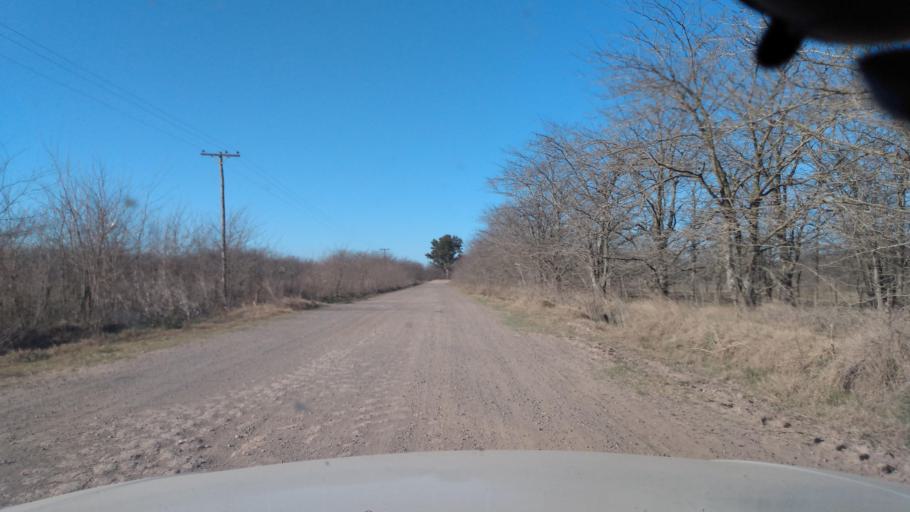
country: AR
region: Buenos Aires
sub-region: Partido de Mercedes
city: Mercedes
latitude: -34.6134
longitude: -59.3282
